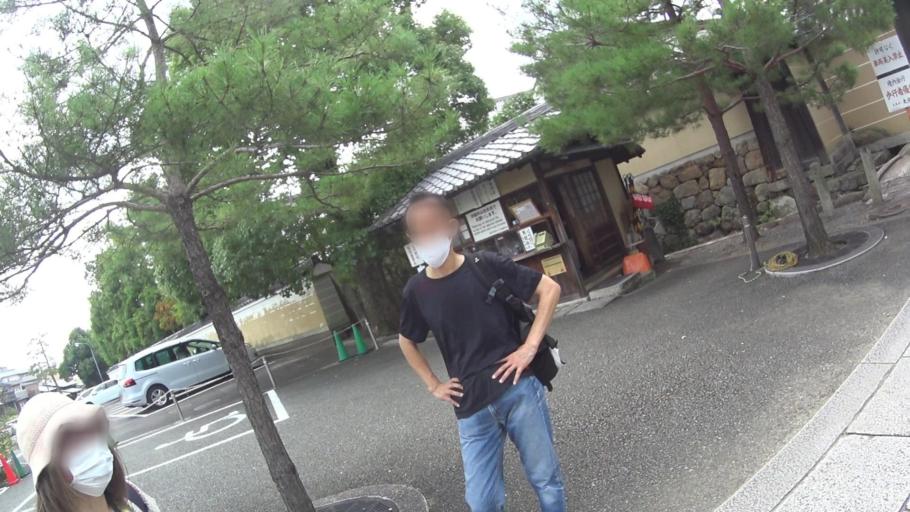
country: JP
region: Kyoto
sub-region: Kyoto-shi
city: Kamigyo-ku
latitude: 35.0456
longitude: 135.7458
